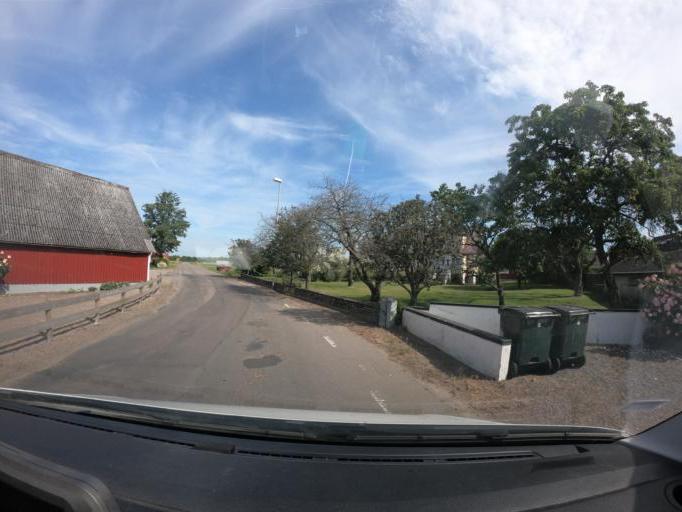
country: SE
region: Skane
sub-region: Angelholms Kommun
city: Vejbystrand
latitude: 56.3972
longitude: 12.6685
